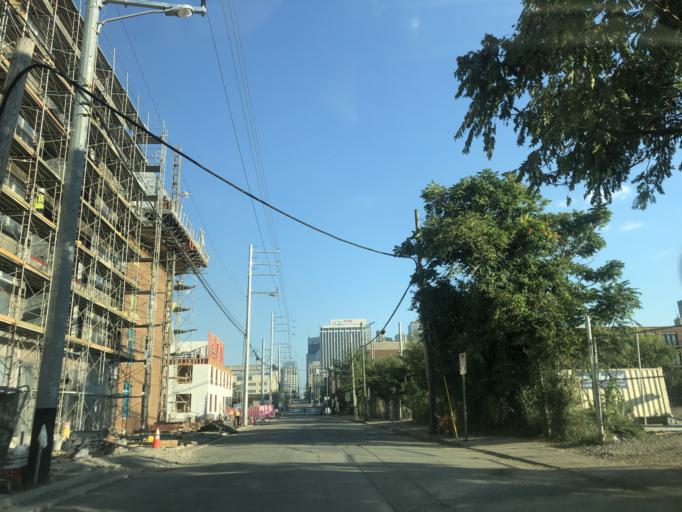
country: US
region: Tennessee
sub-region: Davidson County
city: Nashville
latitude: 36.1727
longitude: -86.7832
